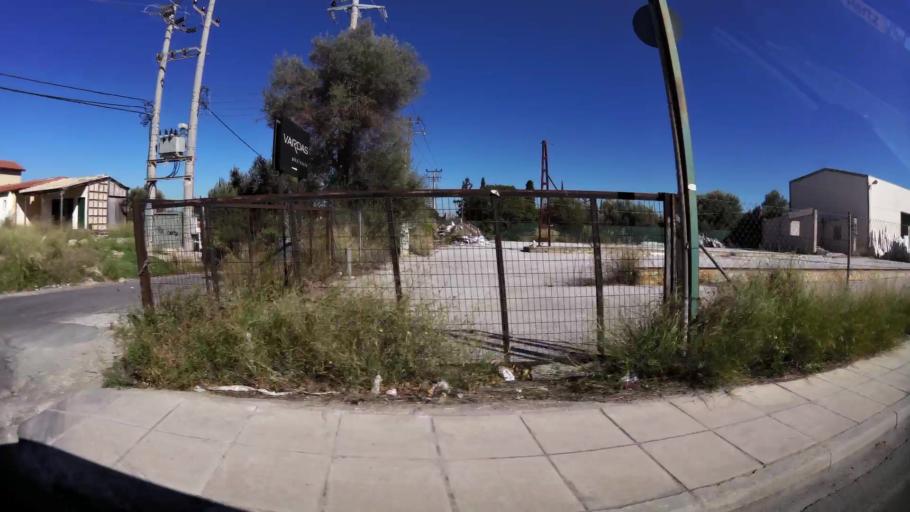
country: GR
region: Attica
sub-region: Nomarchia Anatolikis Attikis
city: Leondarion
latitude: 37.9767
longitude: 23.8534
